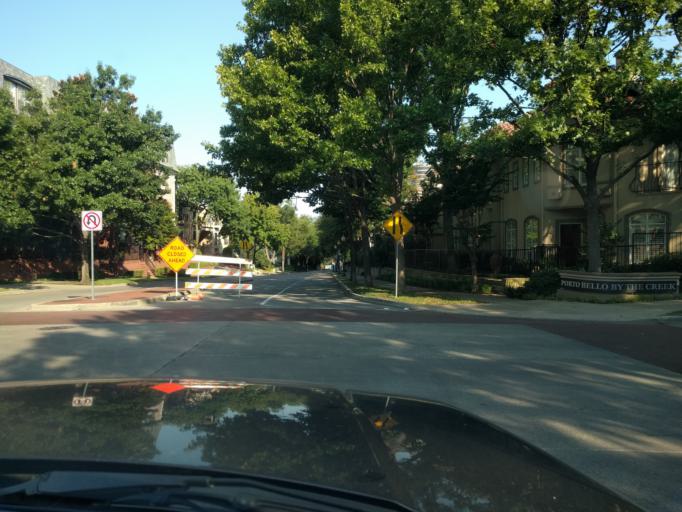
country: US
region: Texas
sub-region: Dallas County
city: Highland Park
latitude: 32.8104
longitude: -96.7976
